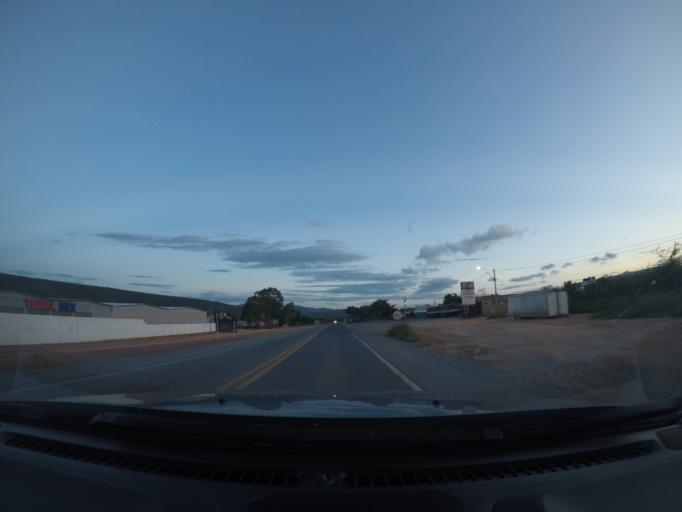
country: BR
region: Bahia
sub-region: Seabra
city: Seabra
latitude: -12.4648
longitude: -41.7453
